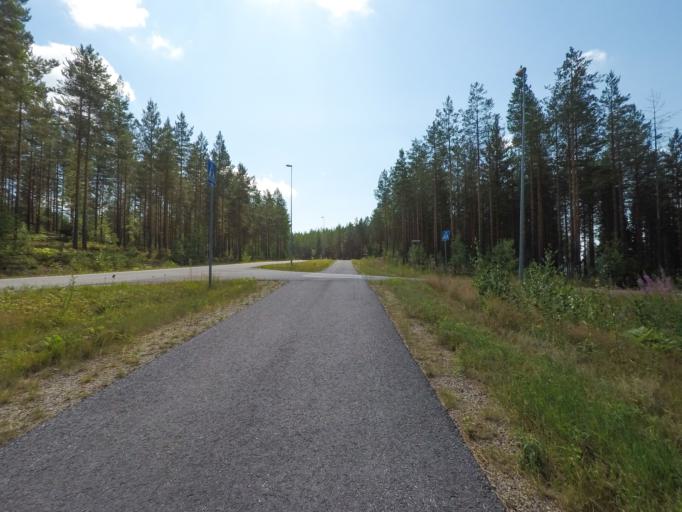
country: FI
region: Southern Savonia
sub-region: Mikkeli
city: Puumala
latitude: 61.5116
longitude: 28.1649
